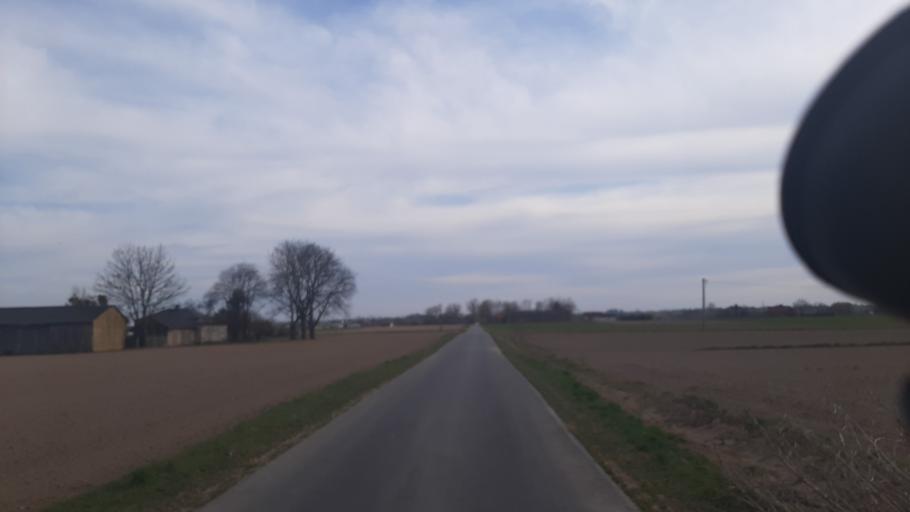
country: PL
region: Lublin Voivodeship
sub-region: Powiat lubelski
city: Jastkow
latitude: 51.3586
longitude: 22.3966
